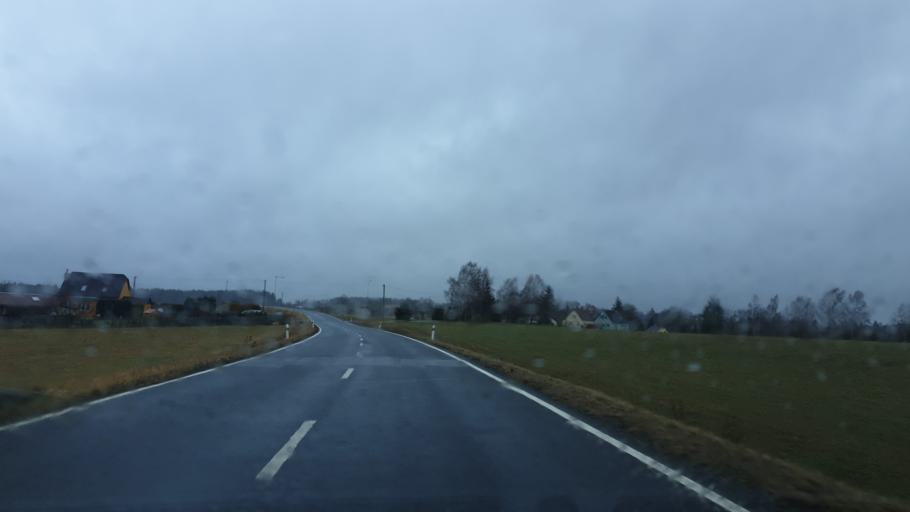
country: CZ
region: Karlovarsky
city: Hranice
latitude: 50.2951
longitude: 12.1763
